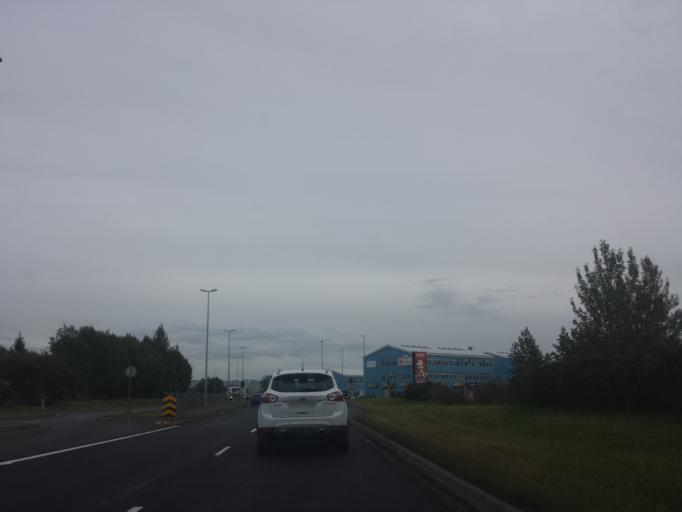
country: IS
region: Capital Region
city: Reykjavik
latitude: 64.1323
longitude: -21.8677
